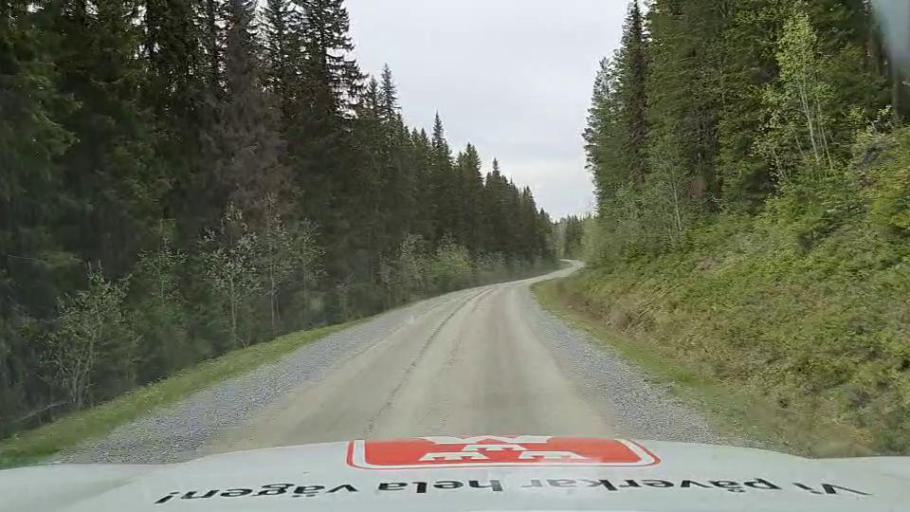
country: SE
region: Jaemtland
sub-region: OEstersunds Kommun
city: Brunflo
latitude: 62.6366
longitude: 14.9355
